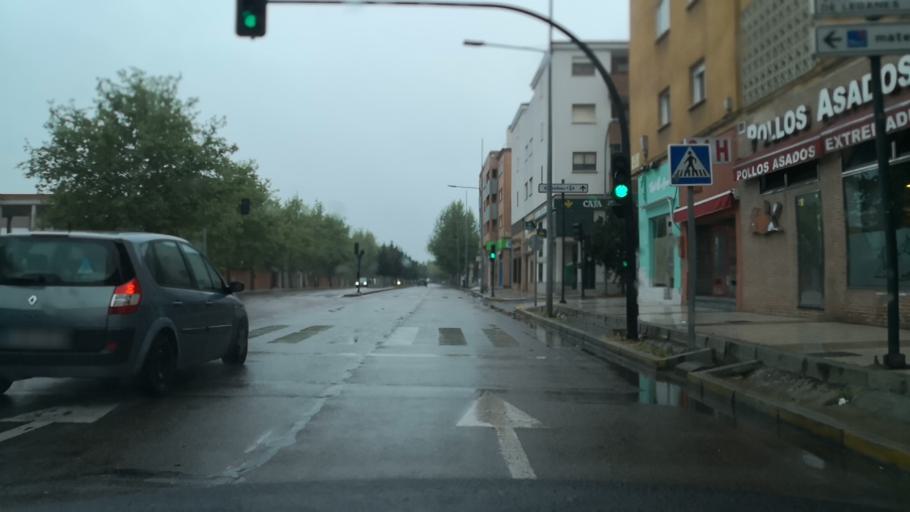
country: ES
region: Extremadura
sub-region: Provincia de Badajoz
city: Badajoz
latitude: 38.8658
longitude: -6.9730
